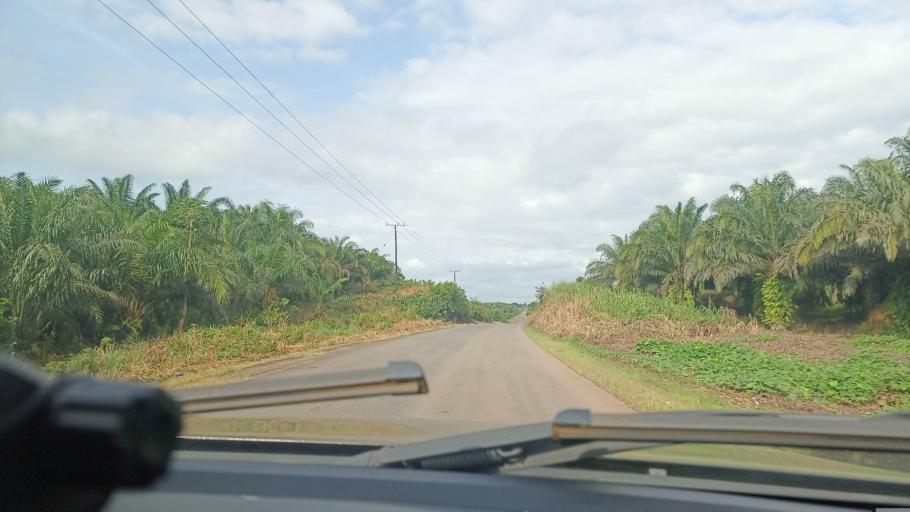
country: LR
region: Bomi
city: Tubmanburg
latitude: 6.7119
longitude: -10.9497
